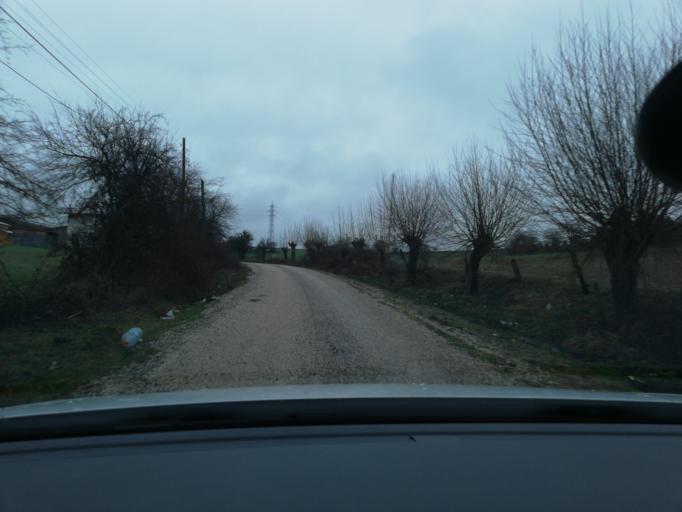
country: TR
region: Bolu
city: Bolu
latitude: 40.7672
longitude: 31.6547
